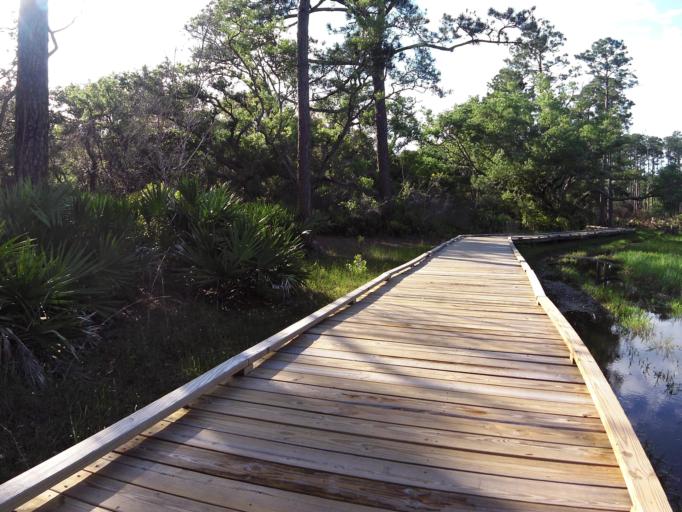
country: US
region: Florida
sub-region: Saint Johns County
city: Villano Beach
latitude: 30.0235
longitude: -81.3382
